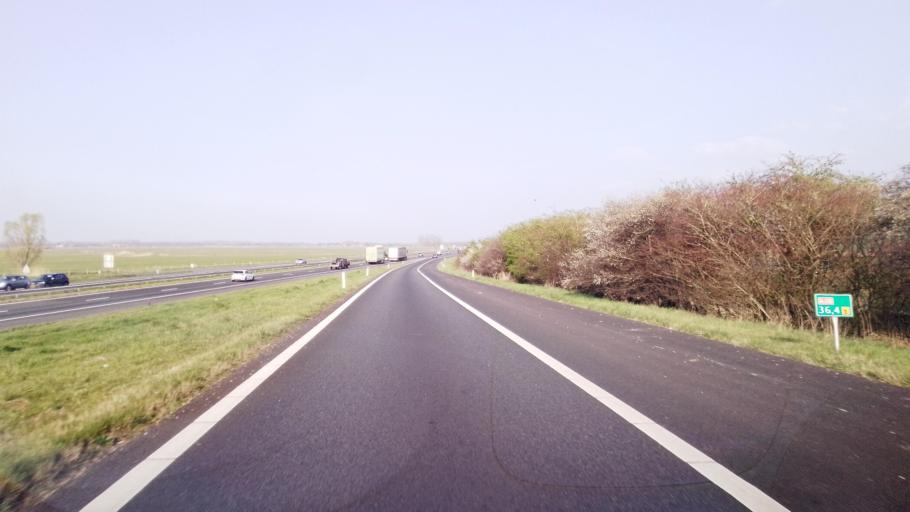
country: NL
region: Gelderland
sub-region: Gemeente Nijkerk
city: Nijkerk
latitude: 52.2443
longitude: 5.4825
